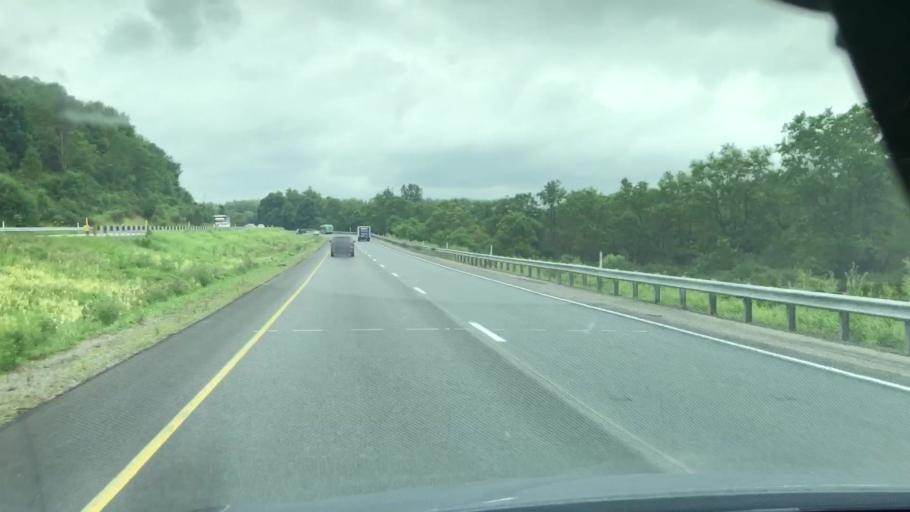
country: US
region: Pennsylvania
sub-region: Butler County
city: Zelienople
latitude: 40.8475
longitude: -80.1027
